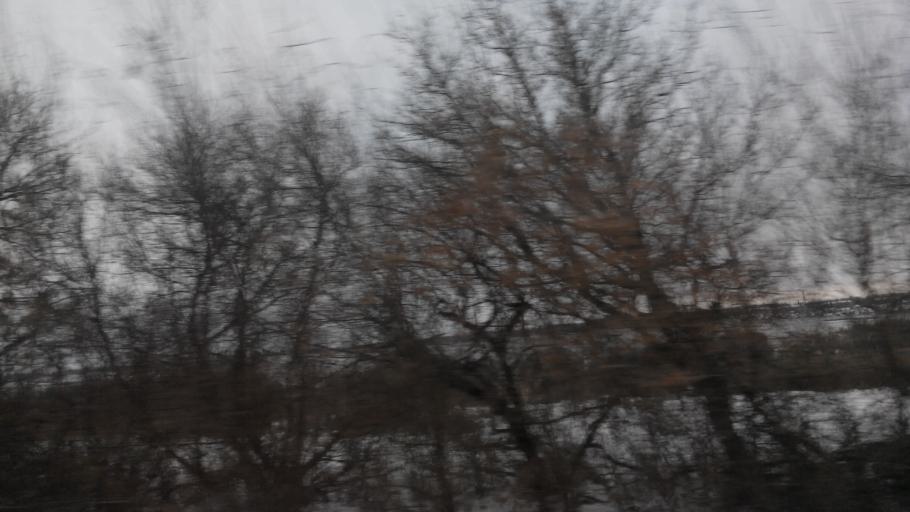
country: RU
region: Tula
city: Mayskiy
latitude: 53.9846
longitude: 38.2132
